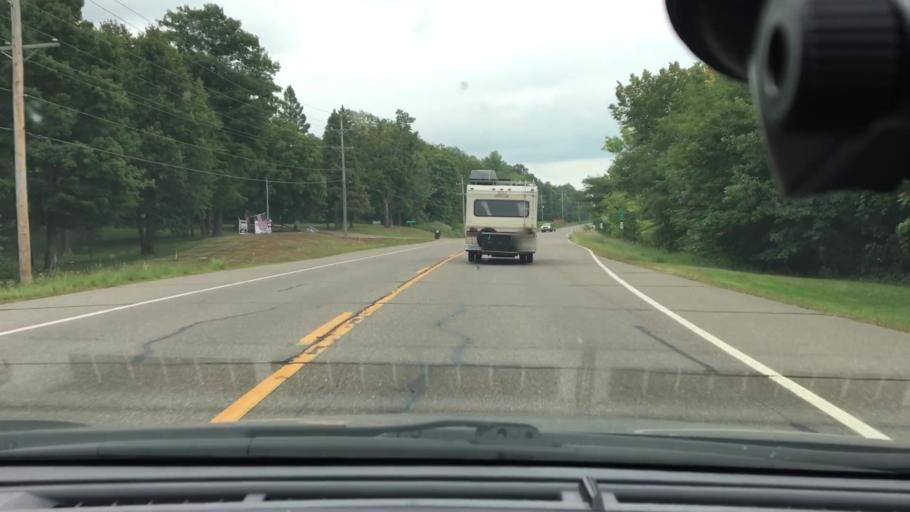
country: US
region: Minnesota
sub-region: Crow Wing County
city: Crosby
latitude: 46.4914
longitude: -93.9174
